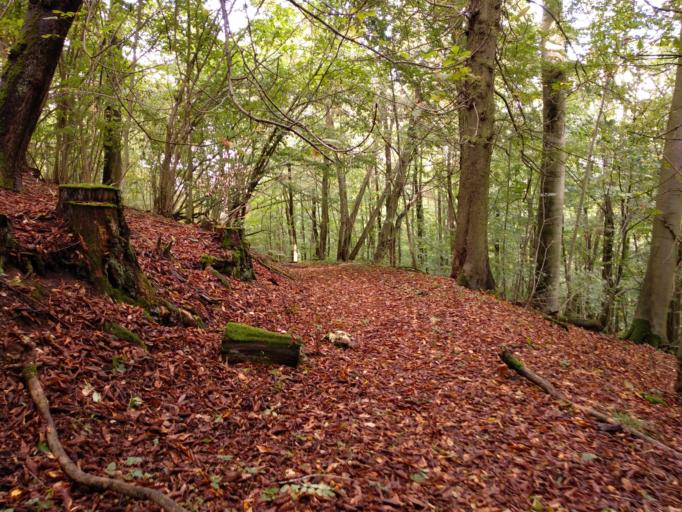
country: DE
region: North Rhine-Westphalia
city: Beverungen
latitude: 51.6525
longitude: 9.3663
